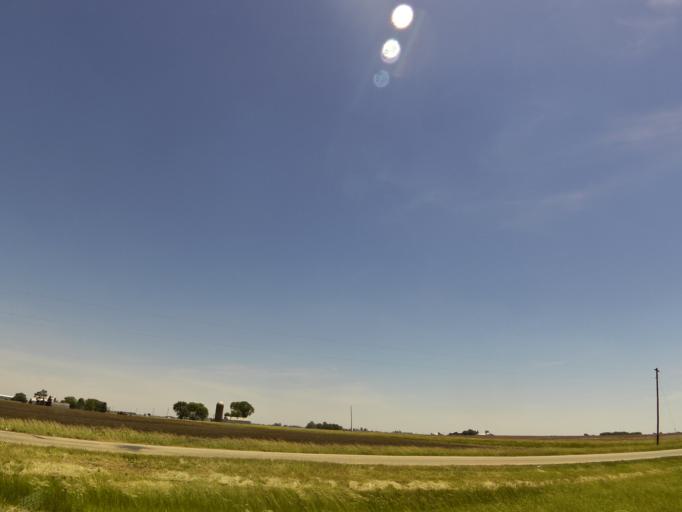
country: US
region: Illinois
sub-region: Iroquois County
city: Onarga
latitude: 40.6832
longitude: -87.8596
